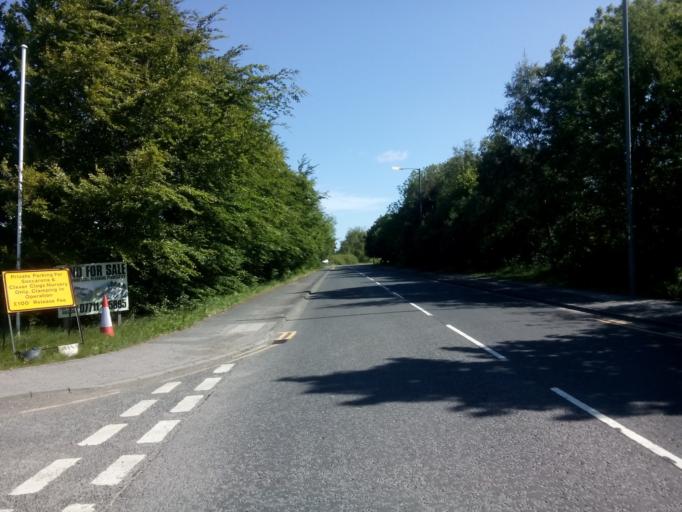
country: GB
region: England
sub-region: County Durham
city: Durham
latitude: 54.7878
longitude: -1.5411
